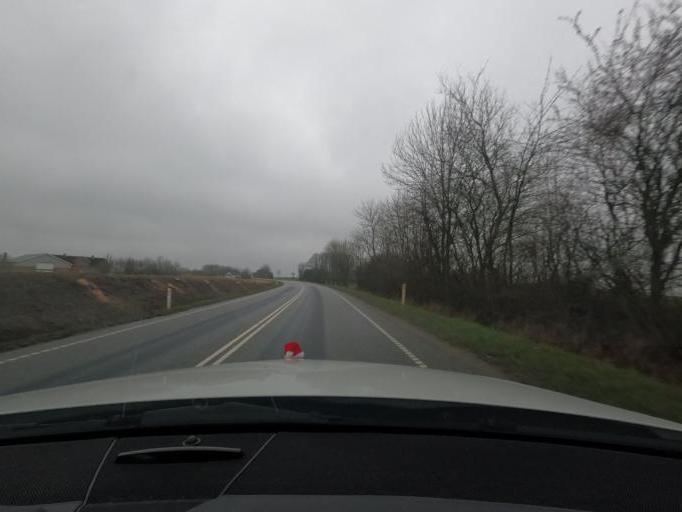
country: DK
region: South Denmark
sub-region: Haderslev Kommune
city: Starup
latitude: 55.2050
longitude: 9.5491
